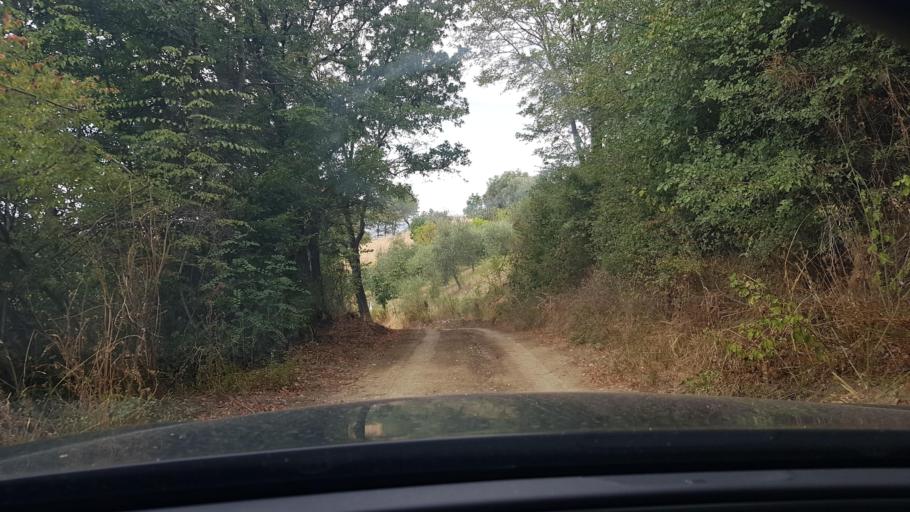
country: AL
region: Durres
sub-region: Rrethi i Durresit
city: Gjepalaj
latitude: 41.3001
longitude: 19.5557
